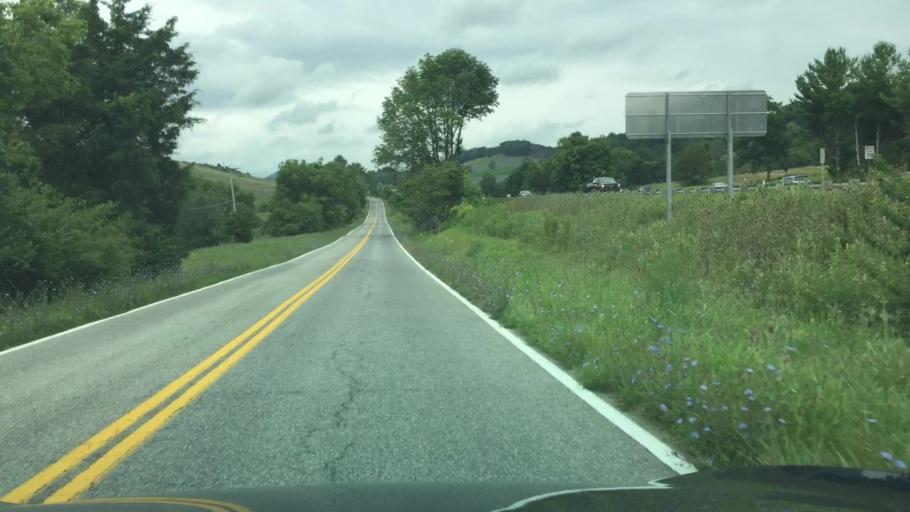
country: US
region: Virginia
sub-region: Pulaski County
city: Pulaski
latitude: 37.0017
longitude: -80.7655
